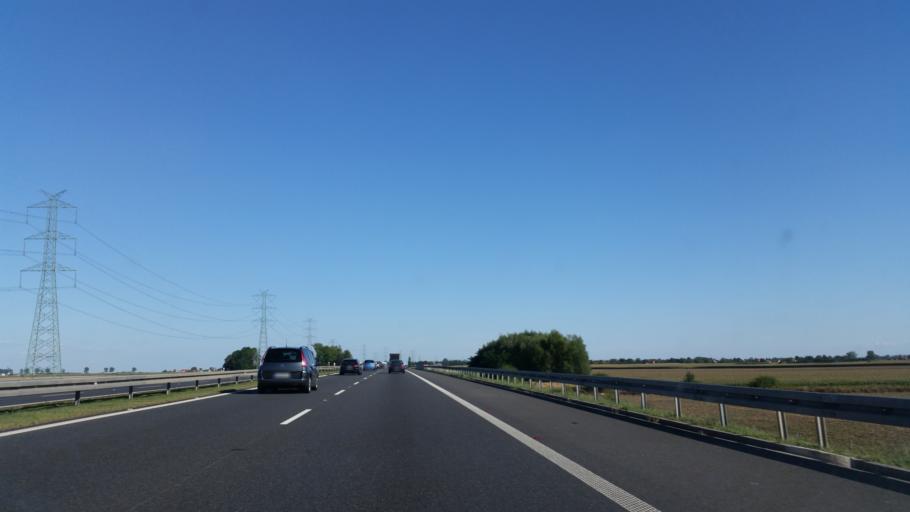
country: PL
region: Lower Silesian Voivodeship
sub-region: Powiat olawski
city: Wierzbno
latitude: 50.9046
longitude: 17.1631
